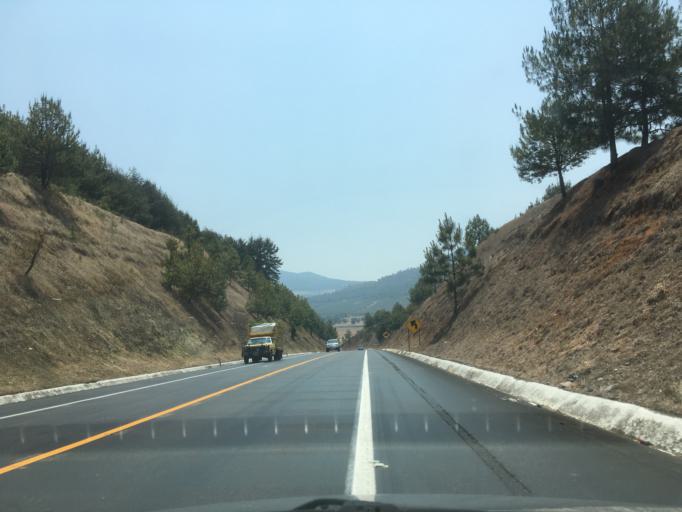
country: MX
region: Michoacan
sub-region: Patzcuaro
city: Santa Maria Huiramangaro (San Juan Tumbio)
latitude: 19.4804
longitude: -101.7393
